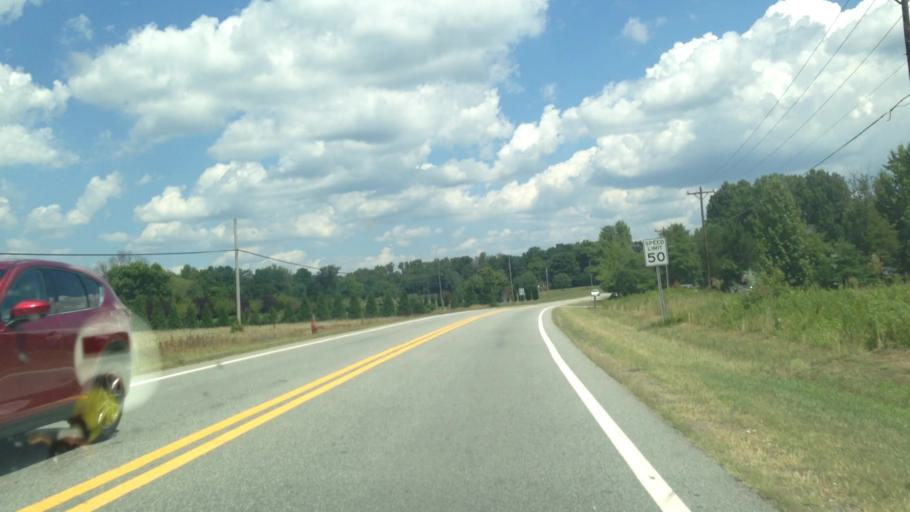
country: US
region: North Carolina
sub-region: Guilford County
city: Stokesdale
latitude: 36.2193
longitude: -79.9914
